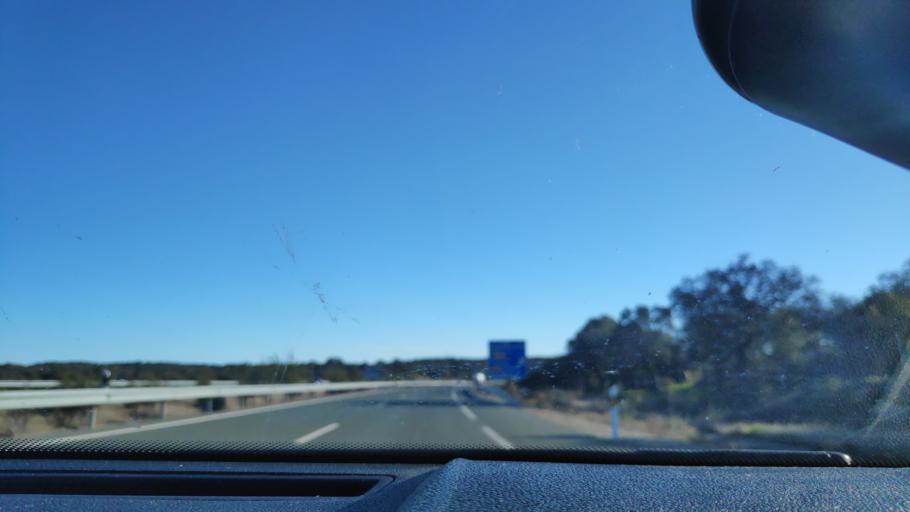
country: ES
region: Andalusia
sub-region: Provincia de Huelva
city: Santa Olalla del Cala
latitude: 37.9118
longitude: -6.2162
